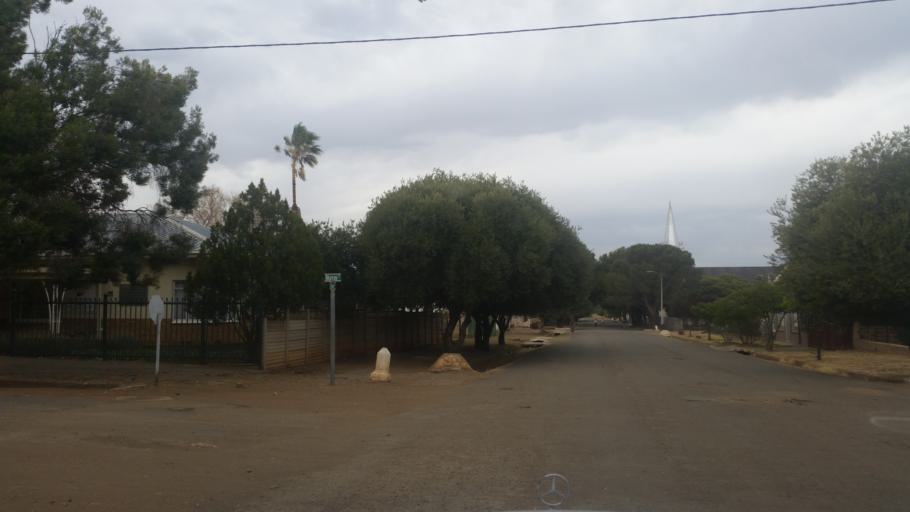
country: ZA
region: Orange Free State
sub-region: Xhariep District Municipality
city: Trompsburg
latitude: -30.4963
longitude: 25.9719
